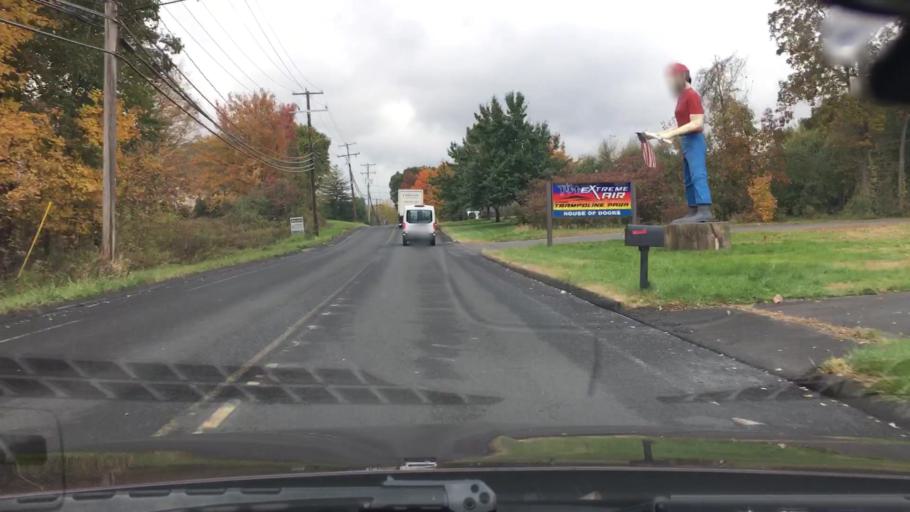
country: US
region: Connecticut
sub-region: New Haven County
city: Cheshire Village
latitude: 41.5562
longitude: -72.9069
